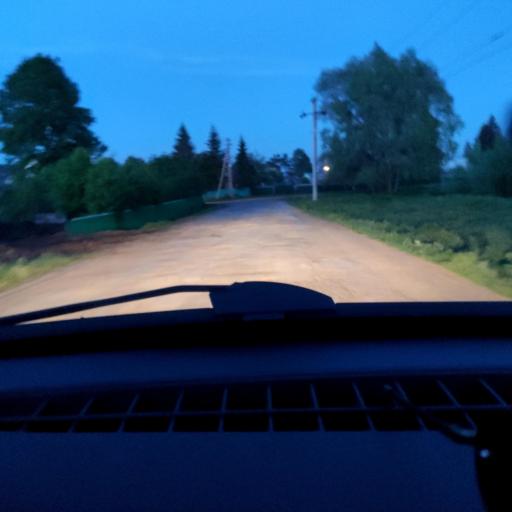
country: RU
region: Bashkortostan
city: Karmaskaly
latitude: 54.3689
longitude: 56.1616
